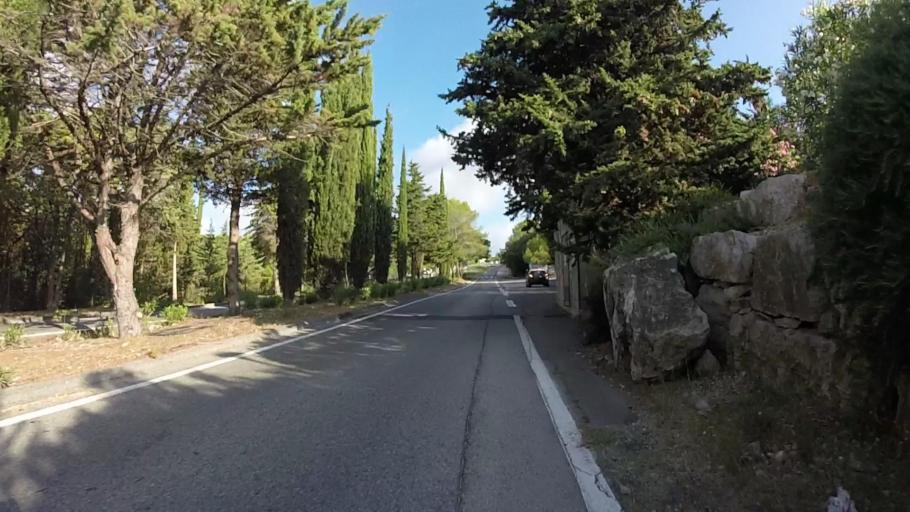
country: FR
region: Provence-Alpes-Cote d'Azur
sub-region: Departement des Alpes-Maritimes
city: Biot
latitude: 43.6213
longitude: 7.0636
